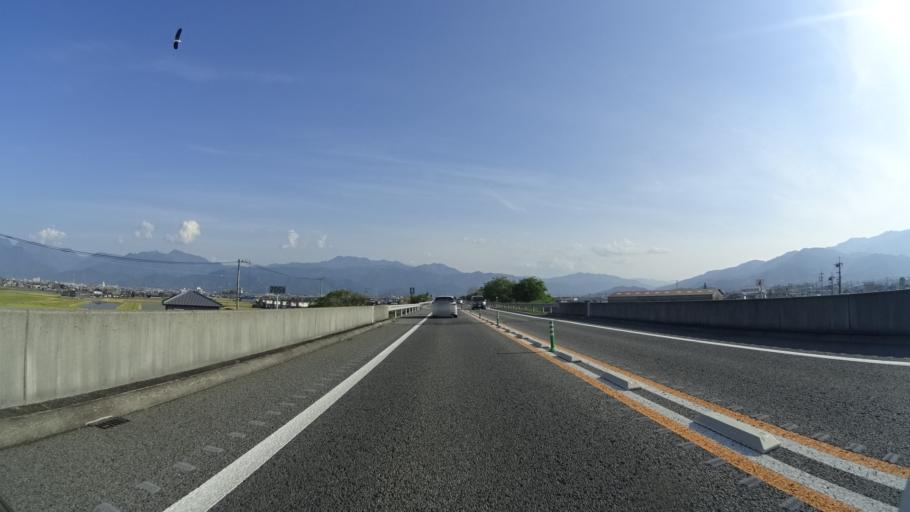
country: JP
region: Ehime
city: Saijo
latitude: 33.9457
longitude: 133.0689
